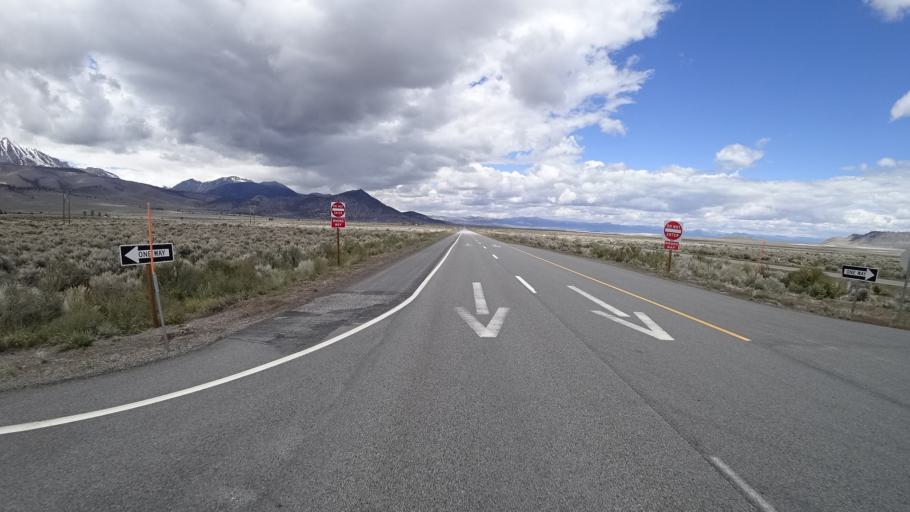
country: US
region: California
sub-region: Mono County
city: Mammoth Lakes
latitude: 37.8744
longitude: -119.0889
